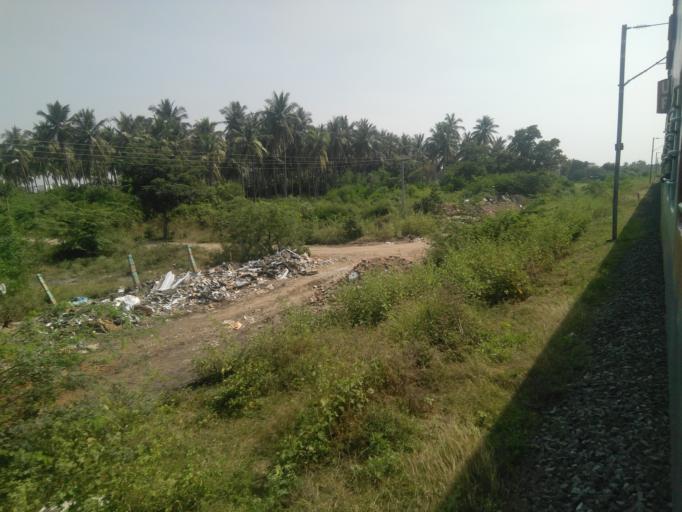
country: IN
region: Tamil Nadu
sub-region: Coimbatore
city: Periyanayakkanpalaiyam
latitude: 11.1185
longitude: 76.9486
